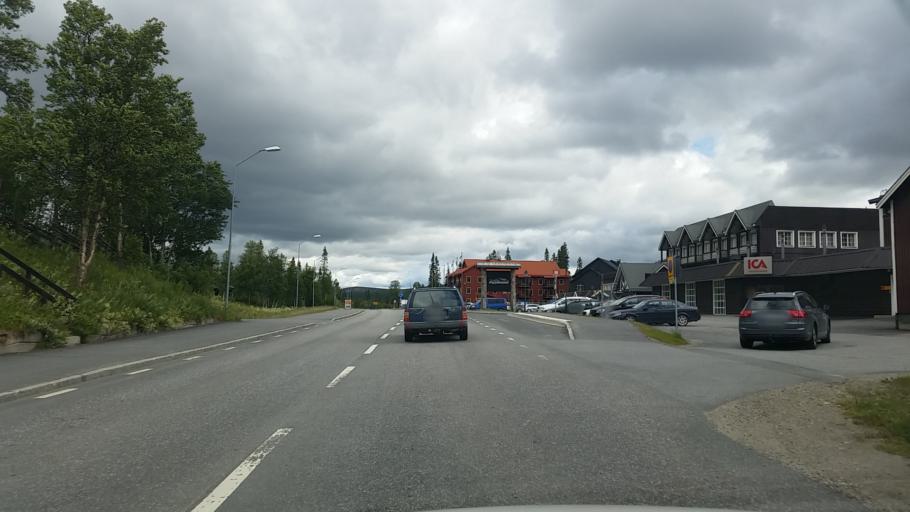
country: SE
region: Jaemtland
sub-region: Bergs Kommun
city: Hoverberg
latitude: 62.4835
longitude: 13.9719
